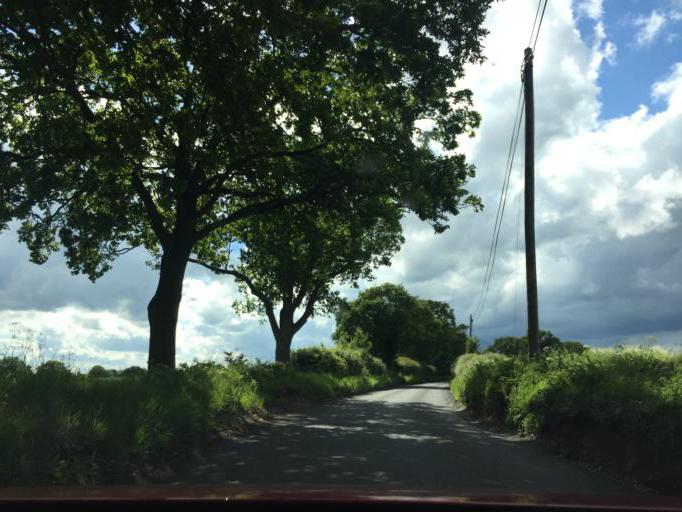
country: GB
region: England
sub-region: Hertfordshire
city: Wheathampstead
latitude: 51.8522
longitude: -0.3158
